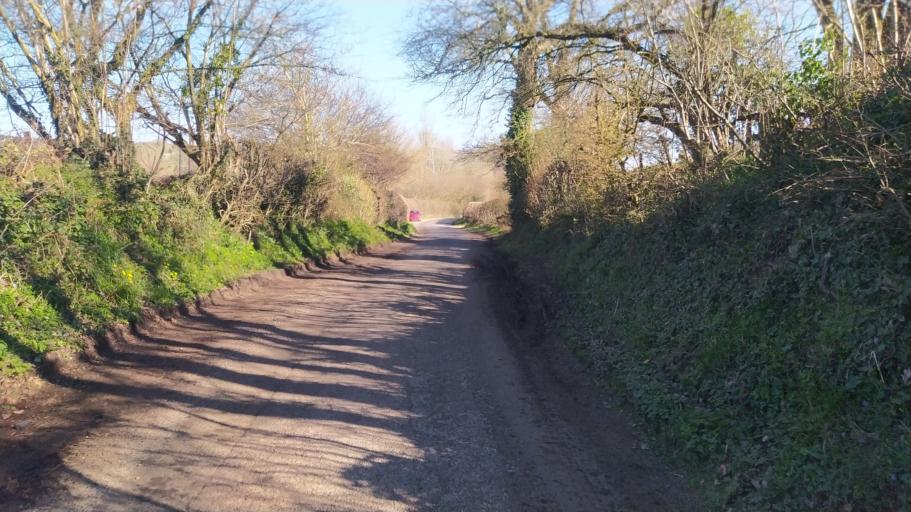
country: GB
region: England
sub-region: Dorset
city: Verwood
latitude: 50.8980
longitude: -1.8964
